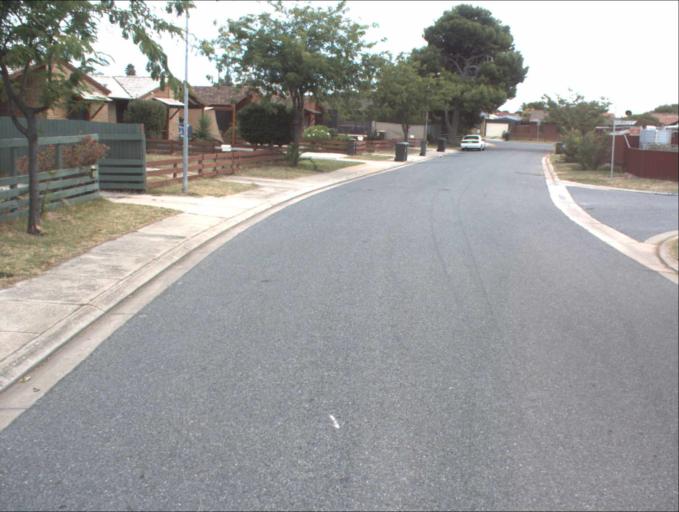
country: AU
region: South Australia
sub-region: Port Adelaide Enfield
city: Birkenhead
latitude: -34.8094
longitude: 138.4982
